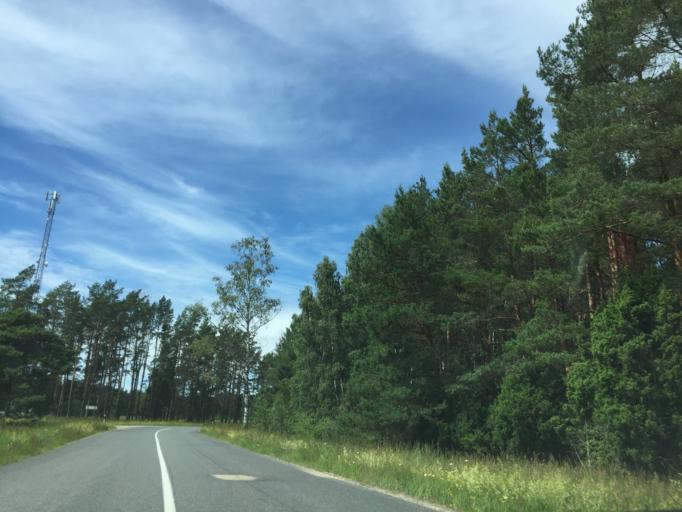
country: LV
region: Dundaga
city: Dundaga
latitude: 57.6283
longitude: 22.5747
